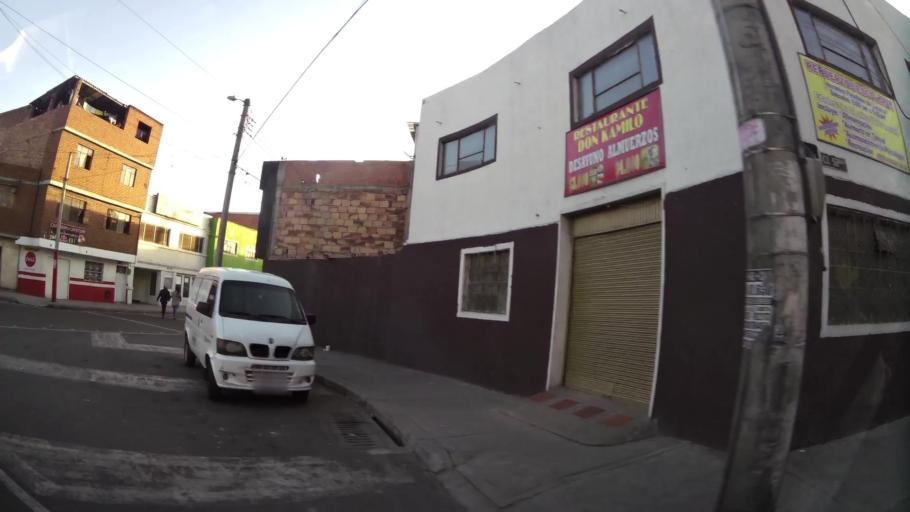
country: CO
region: Bogota D.C.
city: Bogota
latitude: 4.5637
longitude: -74.1263
